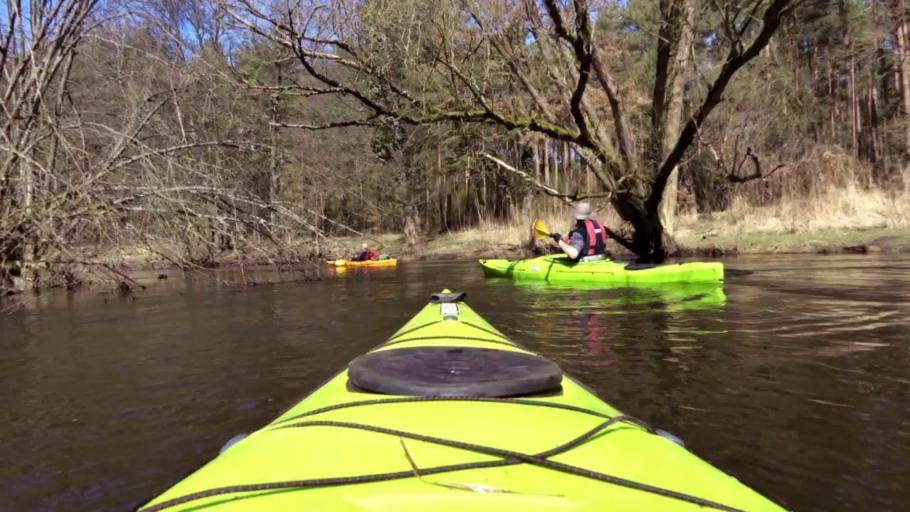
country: PL
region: West Pomeranian Voivodeship
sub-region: Powiat lobeski
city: Lobez
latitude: 53.6526
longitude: 15.5679
